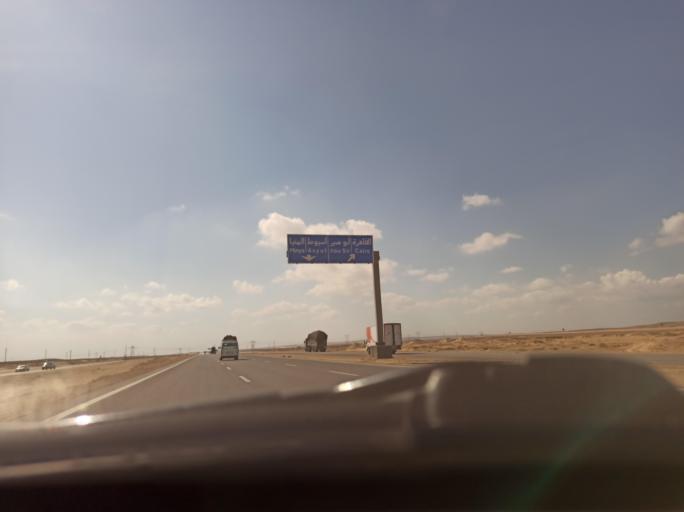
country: EG
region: Muhafazat al Fayyum
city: Al Wasitah
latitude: 29.3232
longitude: 31.0672
